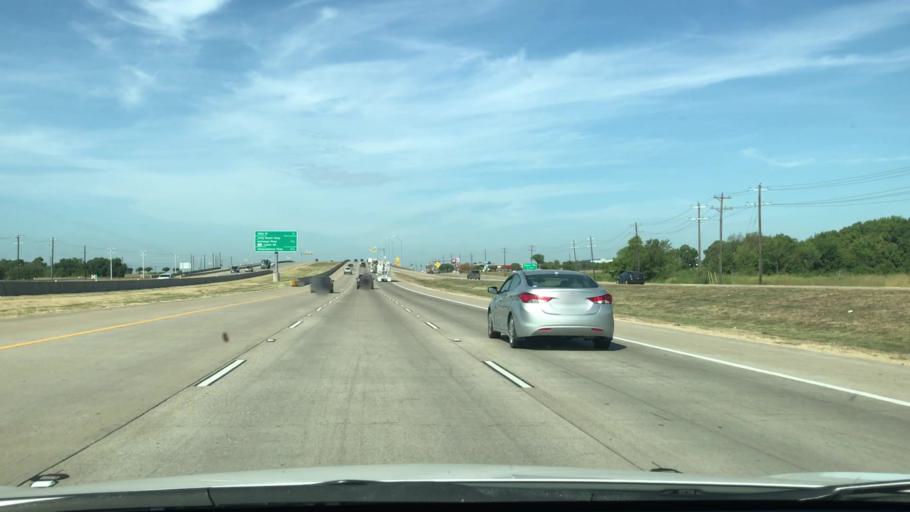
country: US
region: Texas
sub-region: Collin County
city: Allen
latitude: 33.1426
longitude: -96.6852
